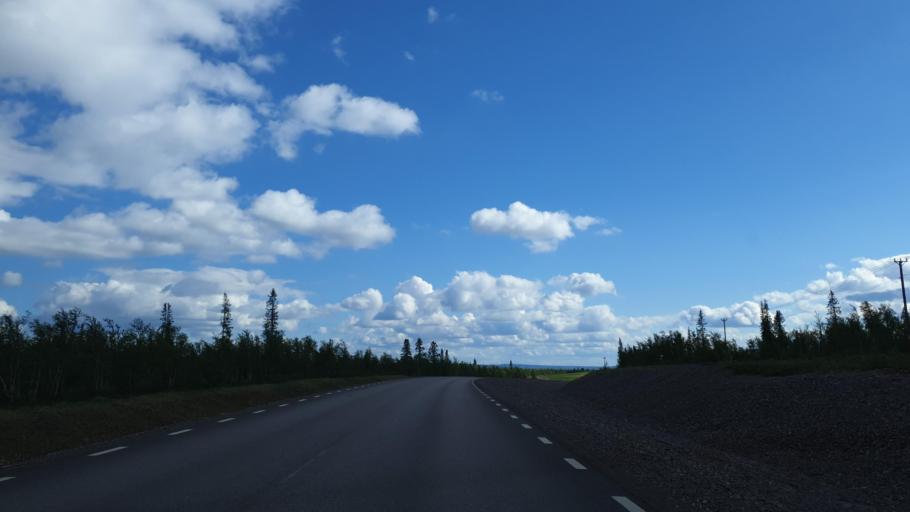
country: SE
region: Norrbotten
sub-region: Kiruna Kommun
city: Kiruna
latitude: 67.8030
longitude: 20.2343
